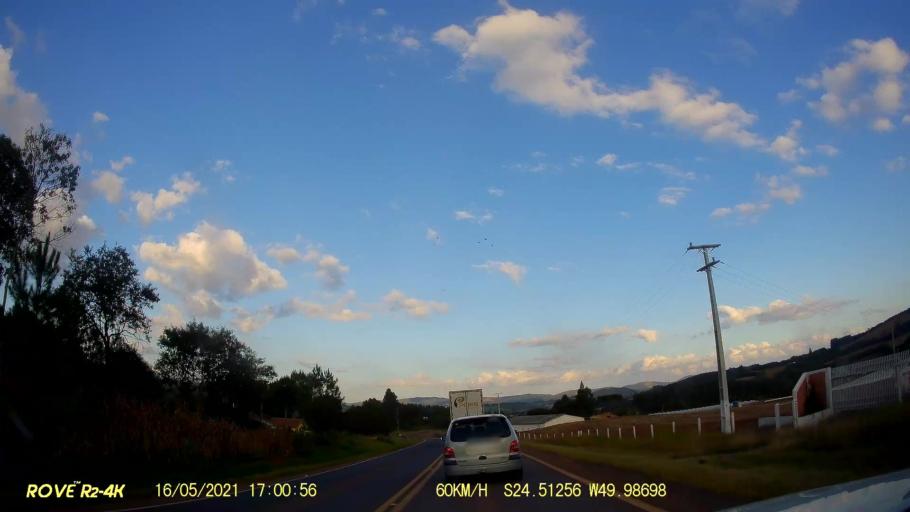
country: BR
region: Parana
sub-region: Pirai Do Sul
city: Pirai do Sul
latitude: -24.5126
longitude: -49.9870
